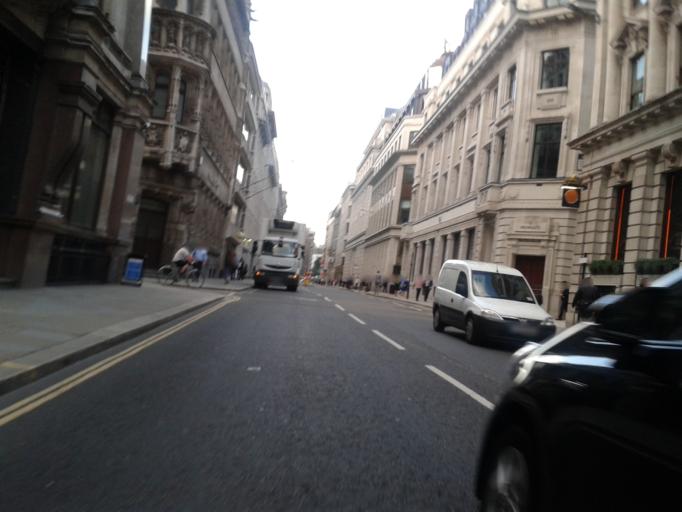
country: GB
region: England
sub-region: Greater London
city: City of London
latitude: 51.5151
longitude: -0.0896
